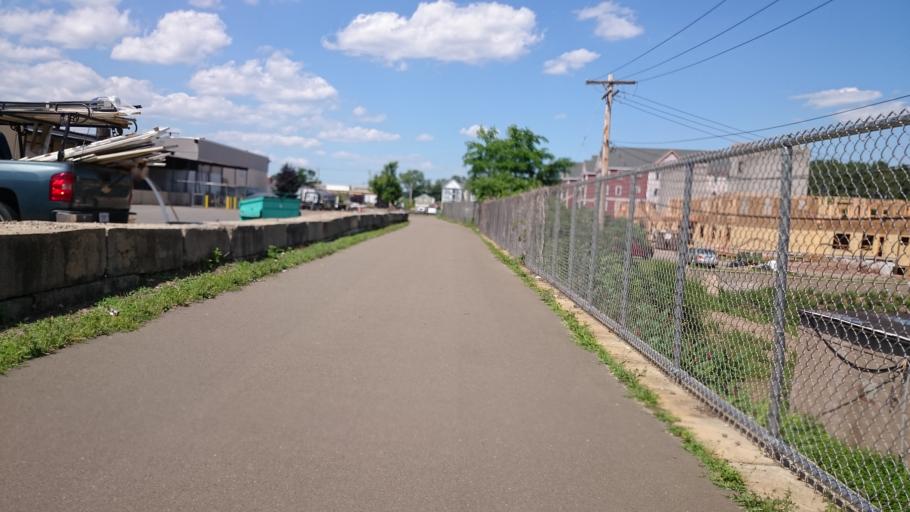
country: US
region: Connecticut
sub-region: New Haven County
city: New Haven
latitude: 41.3546
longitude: -72.9260
